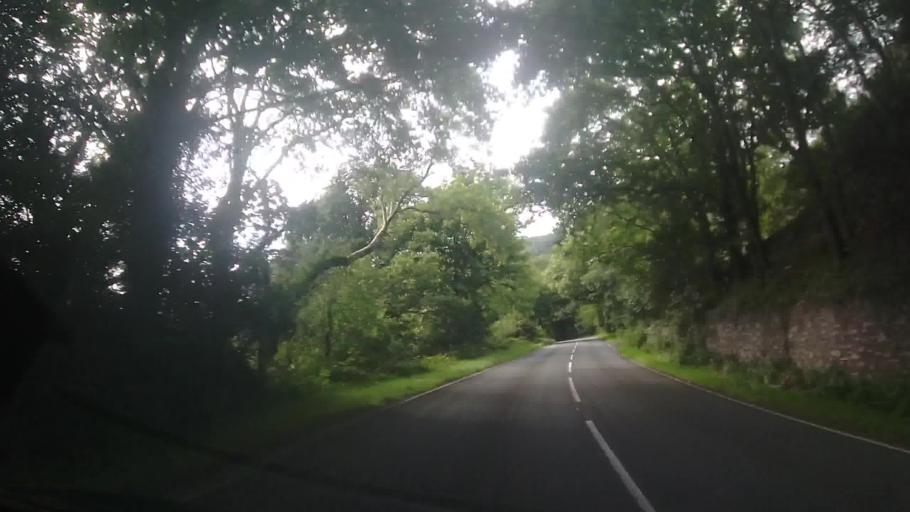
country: GB
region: Wales
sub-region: Gwynedd
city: Barmouth
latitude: 52.7420
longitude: -3.9965
